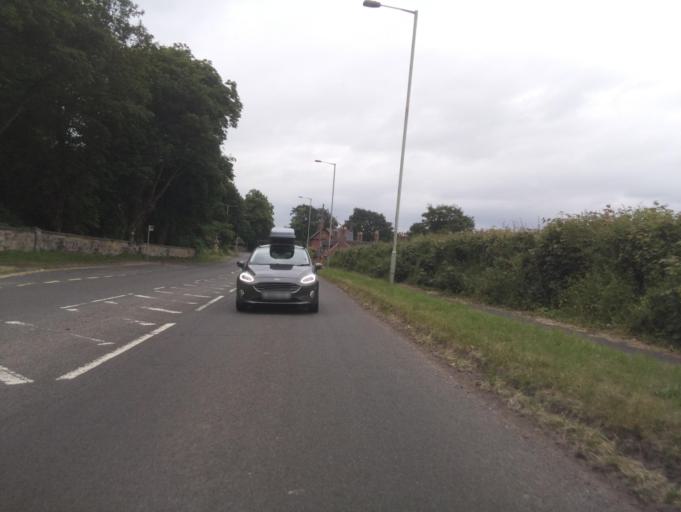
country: GB
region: England
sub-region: Staffordshire
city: Penkridge
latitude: 52.7563
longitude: -2.1073
